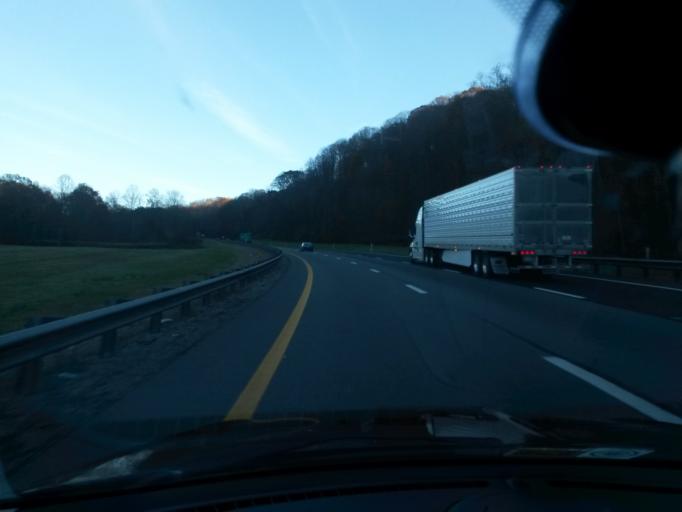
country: US
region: West Virginia
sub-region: Raleigh County
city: Prosperity
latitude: 37.8497
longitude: -81.2514
